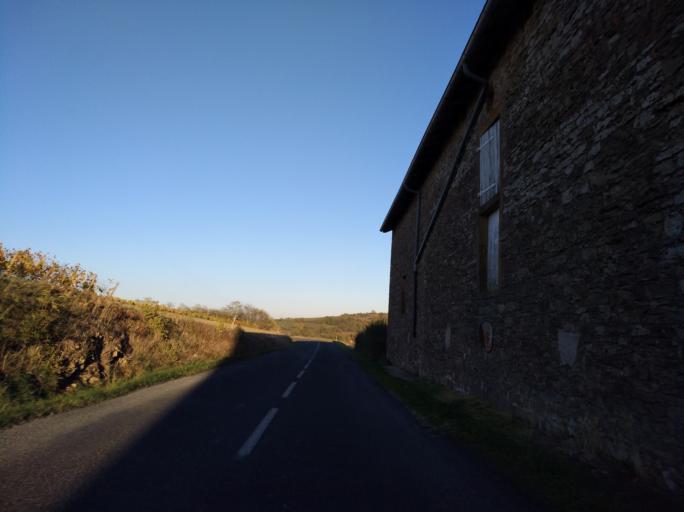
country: FR
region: Rhone-Alpes
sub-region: Departement du Rhone
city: Theize
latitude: 45.9709
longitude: 4.5686
